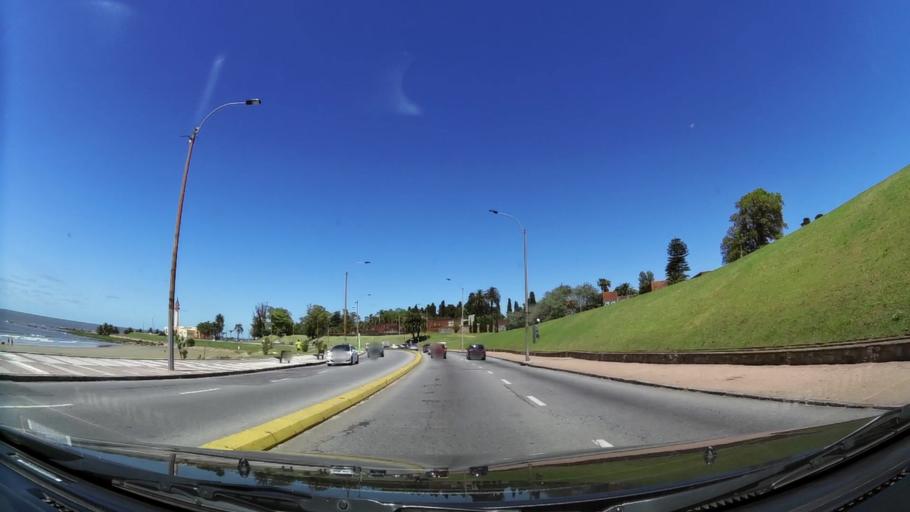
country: UY
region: Montevideo
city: Montevideo
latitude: -34.9003
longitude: -56.1231
